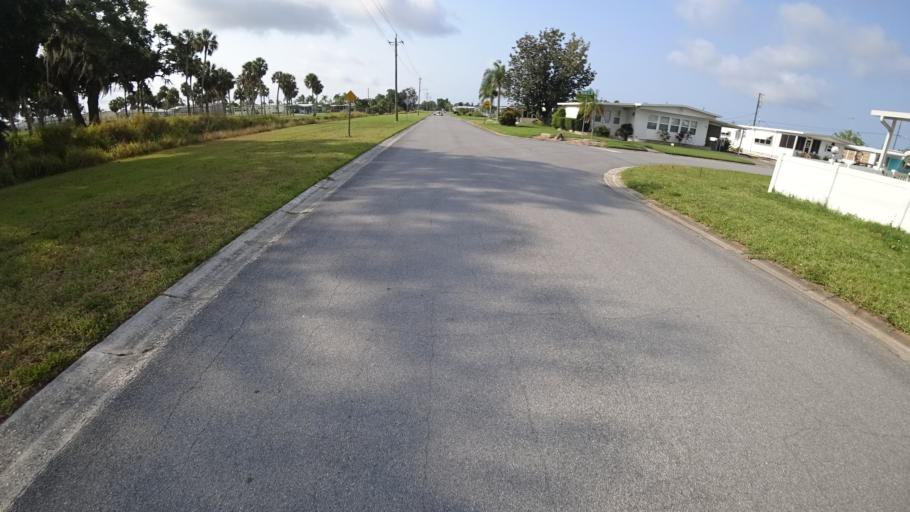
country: US
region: Florida
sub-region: Manatee County
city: West Samoset
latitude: 27.4562
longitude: -82.5632
